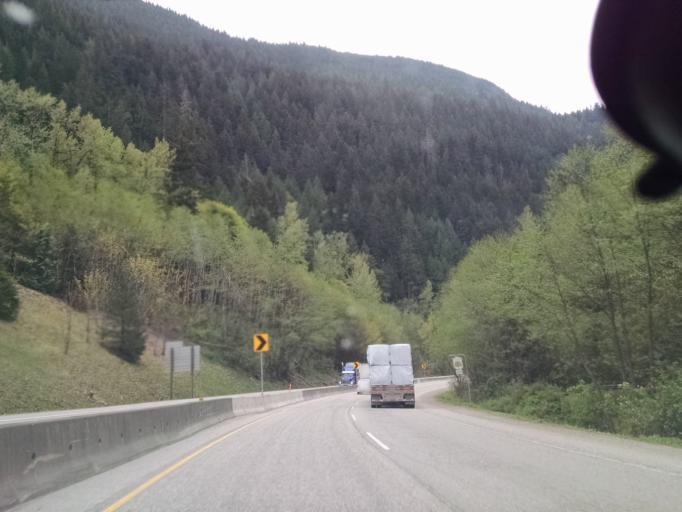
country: CA
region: British Columbia
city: Hope
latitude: 49.3818
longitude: -121.3190
